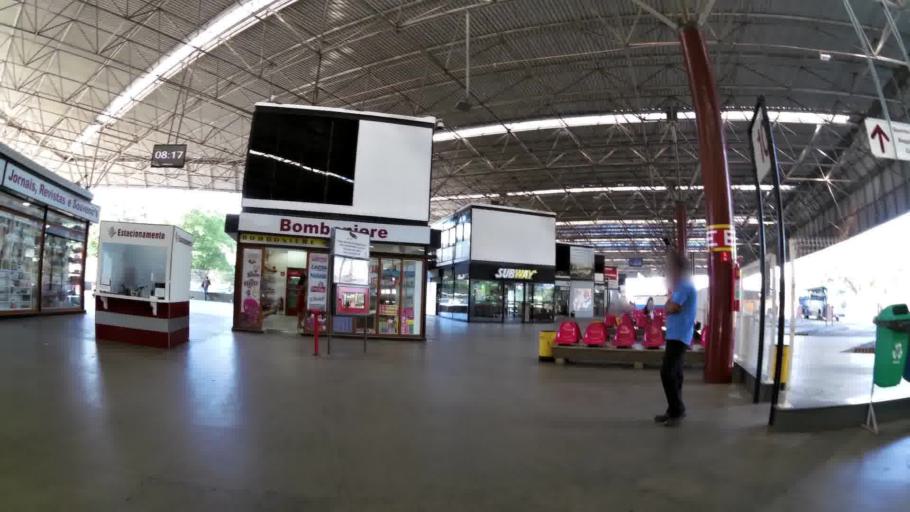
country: BR
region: Espirito Santo
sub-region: Vitoria
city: Vitoria
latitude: -20.3229
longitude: -40.3520
